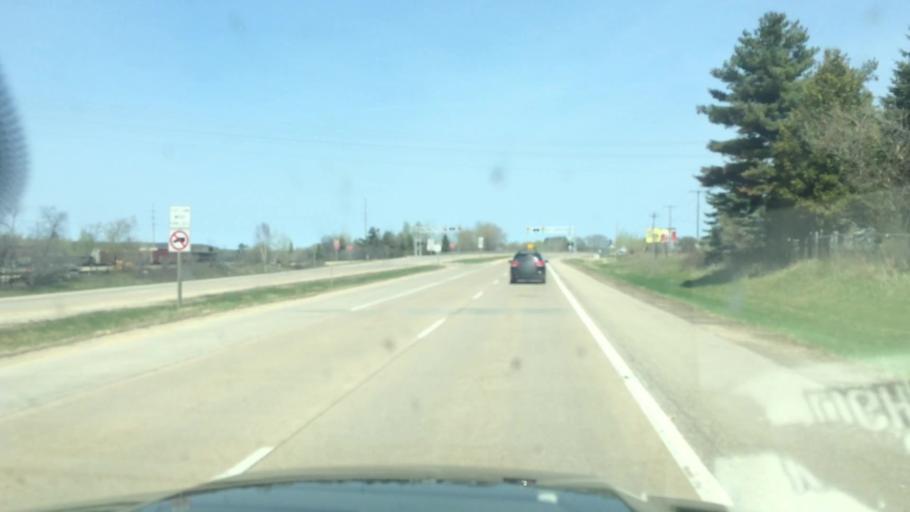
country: US
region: Michigan
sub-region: Delta County
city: Gladstone
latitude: 45.8470
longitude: -87.0291
